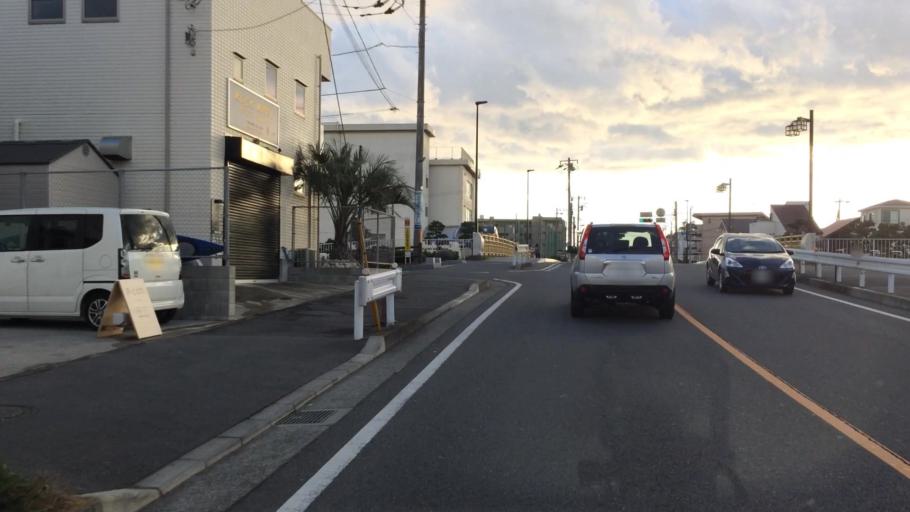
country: JP
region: Kanagawa
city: Fujisawa
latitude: 35.3198
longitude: 139.4639
